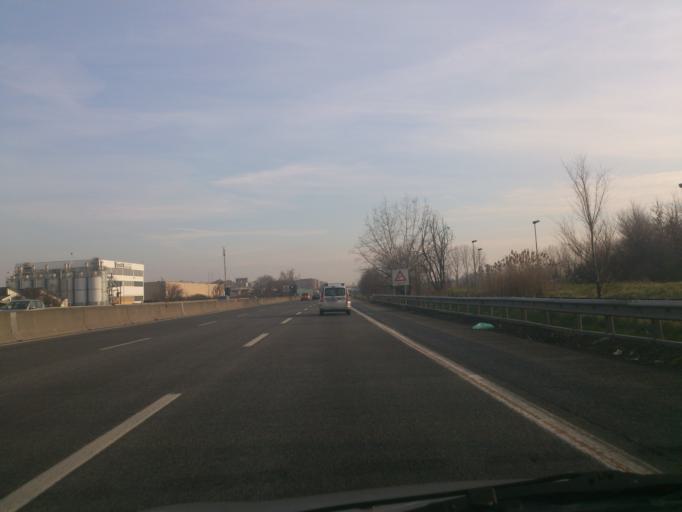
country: IT
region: Lombardy
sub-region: Citta metropolitana di Milano
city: Chiaravalle
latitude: 45.4140
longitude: 9.2531
